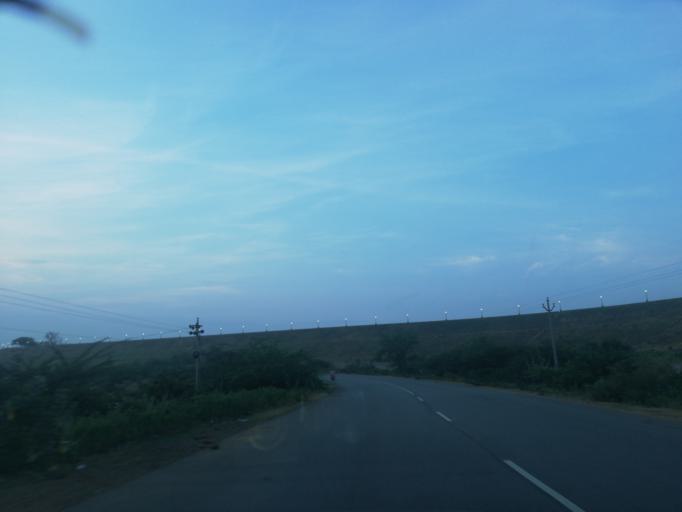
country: IN
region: Andhra Pradesh
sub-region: Guntur
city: Macherla
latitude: 16.5960
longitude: 79.3078
